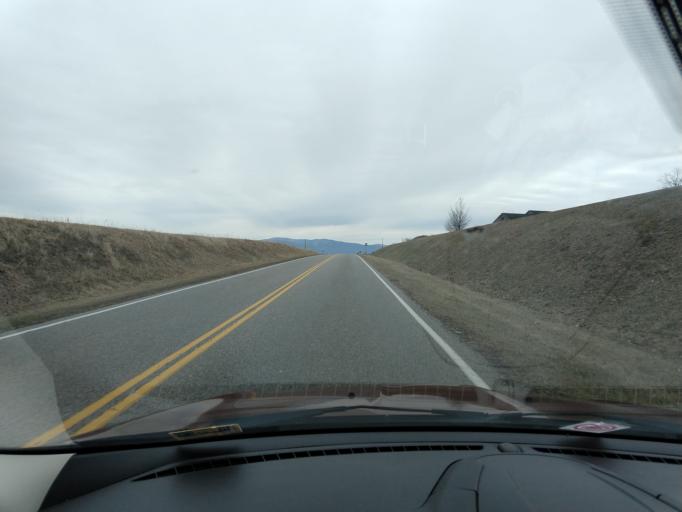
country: US
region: Virginia
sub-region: Augusta County
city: Weyers Cave
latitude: 38.2805
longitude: -78.9022
